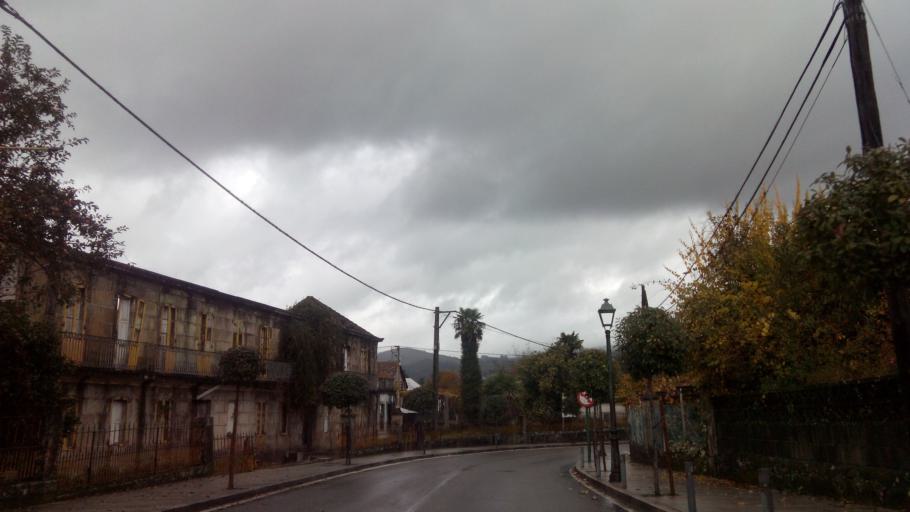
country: ES
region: Galicia
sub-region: Provincia de Pontevedra
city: Mondariz-Balneario
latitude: 42.2263
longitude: -8.4698
